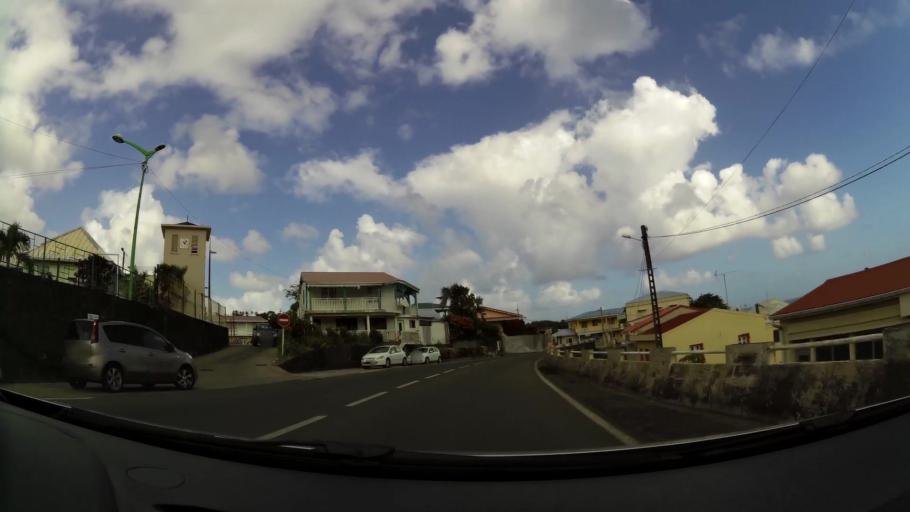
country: MQ
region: Martinique
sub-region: Martinique
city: Le Lorrain
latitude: 14.8215
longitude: -61.0304
